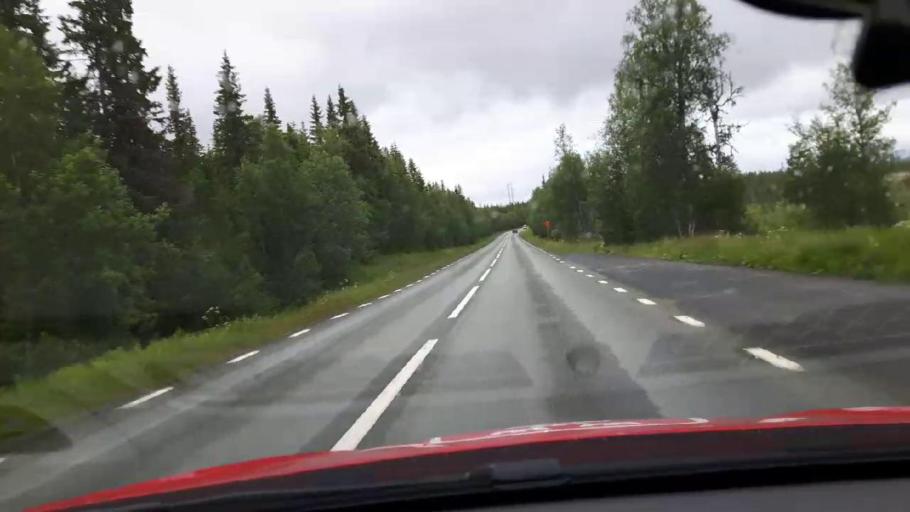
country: SE
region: Jaemtland
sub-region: Are Kommun
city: Are
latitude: 63.3297
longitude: 12.5576
